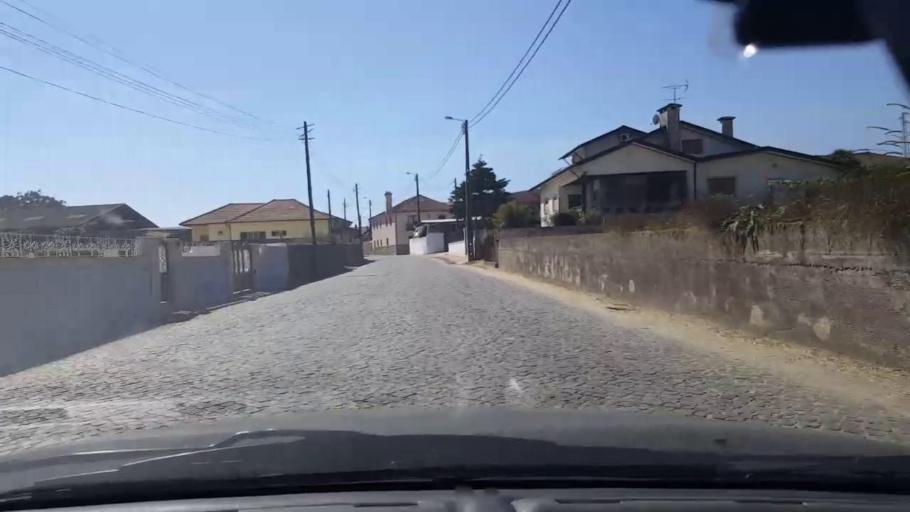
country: PT
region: Porto
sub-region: Matosinhos
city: Lavra
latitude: 41.2790
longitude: -8.7046
